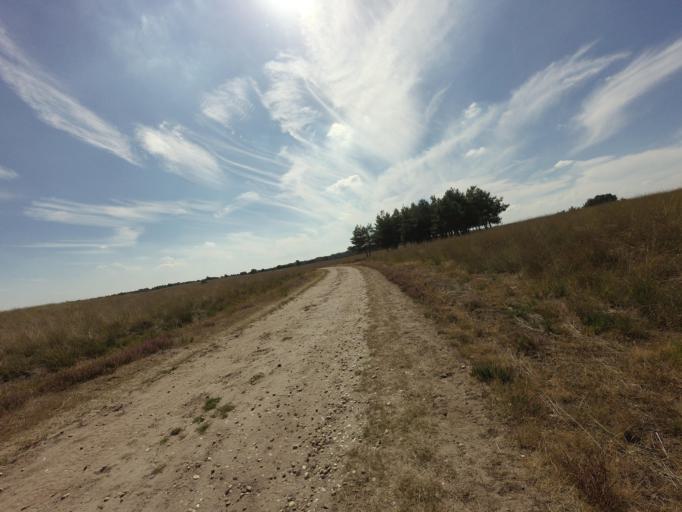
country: NL
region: Gelderland
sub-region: Gemeente Rheden
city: Rheden
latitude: 52.0501
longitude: 5.9977
